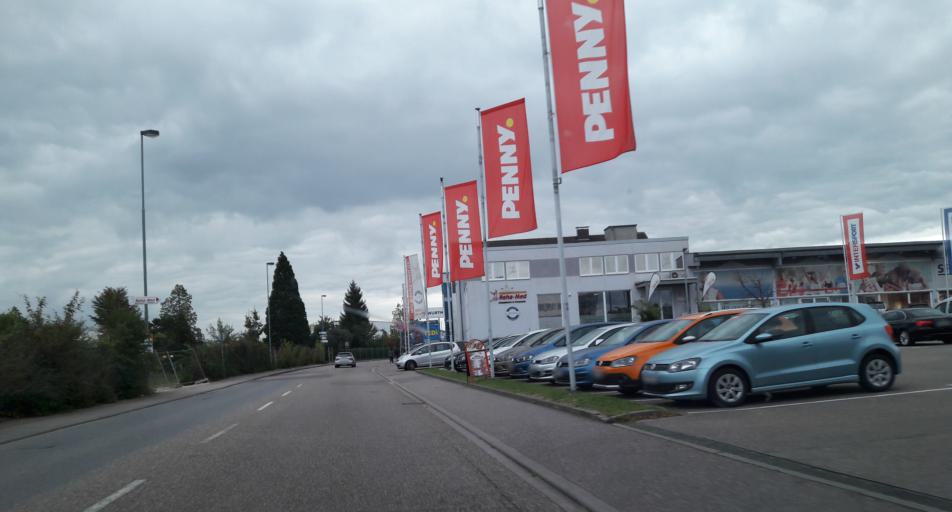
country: DE
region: Baden-Wuerttemberg
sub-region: Karlsruhe Region
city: Sinsheim
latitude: 49.2475
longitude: 8.8806
